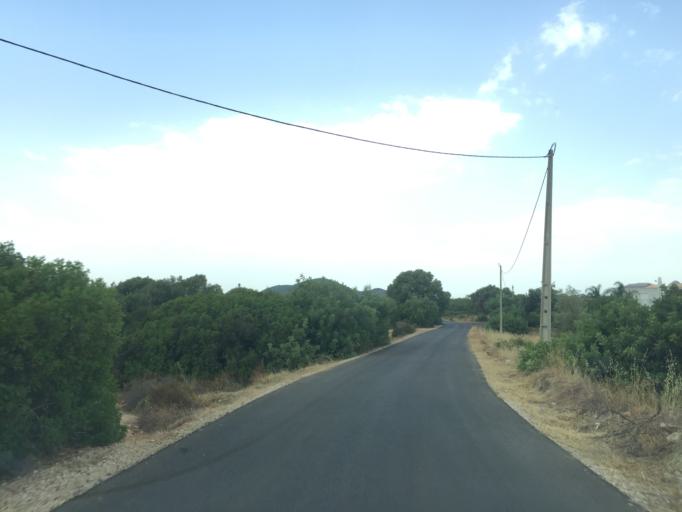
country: PT
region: Faro
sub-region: Loule
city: Almancil
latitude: 37.0967
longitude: -8.0309
